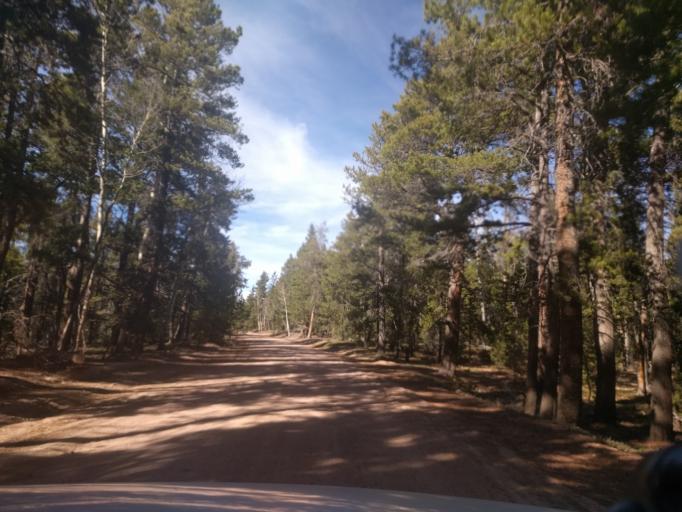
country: US
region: Colorado
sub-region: Douglas County
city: Perry Park
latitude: 39.2129
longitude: -105.0572
